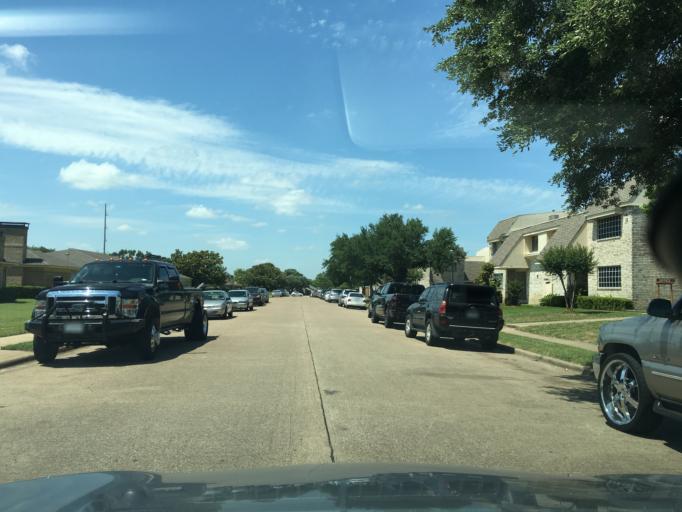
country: US
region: Texas
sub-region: Dallas County
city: Richardson
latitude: 32.9433
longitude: -96.6858
